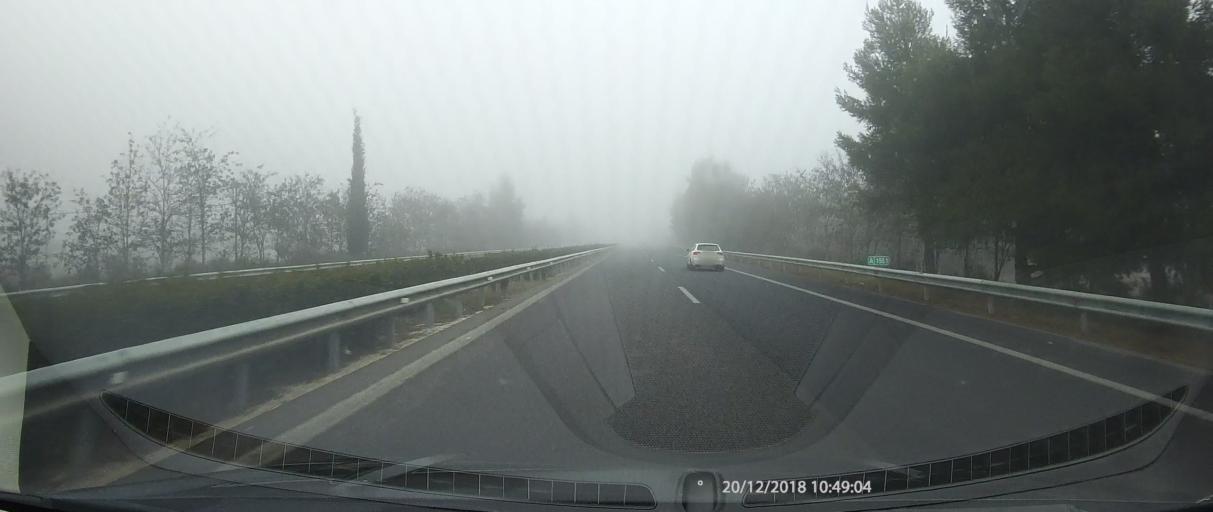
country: GR
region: Peloponnese
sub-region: Nomos Arkadias
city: Tripoli
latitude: 37.5307
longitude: 22.4115
